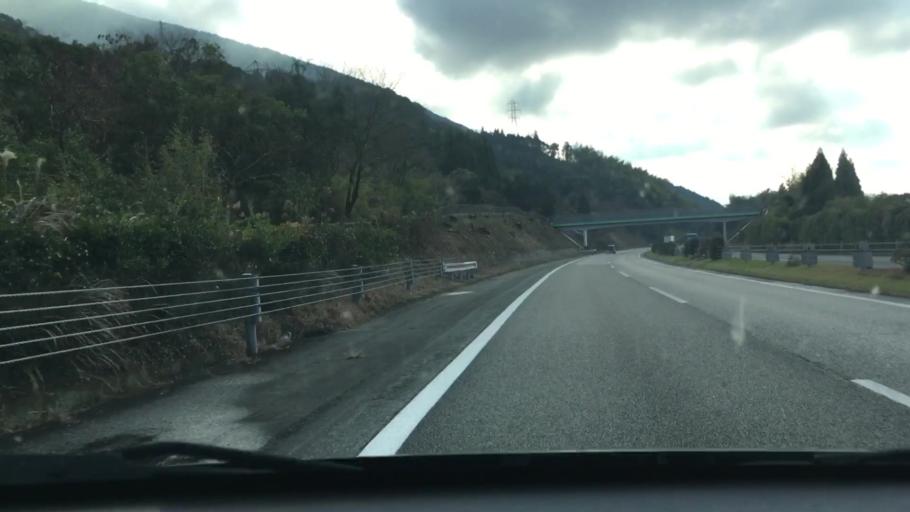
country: JP
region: Kumamoto
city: Yatsushiro
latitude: 32.5343
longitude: 130.6716
